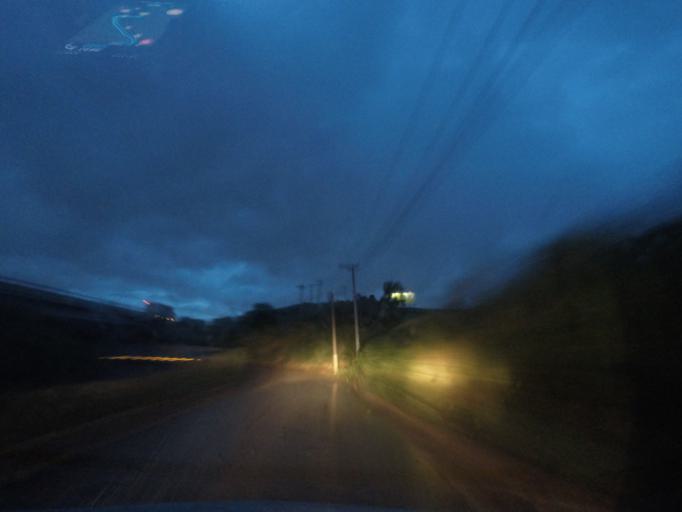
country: BR
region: Sao Paulo
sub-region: Louveira
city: Louveira
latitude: -23.0878
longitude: -47.0202
